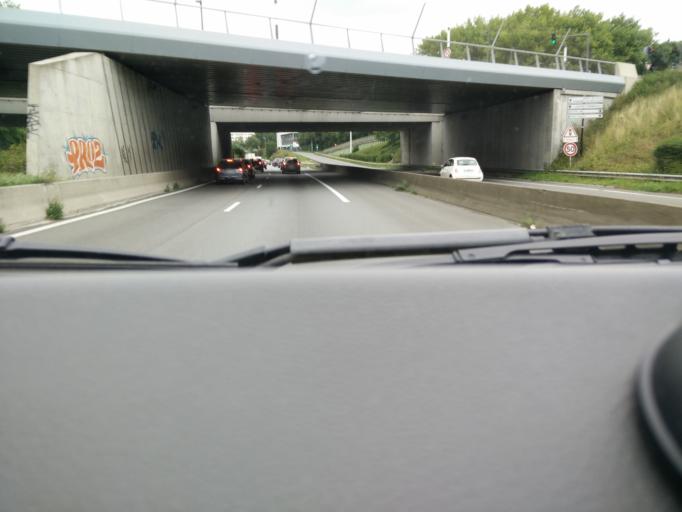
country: FR
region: Nord-Pas-de-Calais
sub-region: Departement du Nord
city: Lezennes
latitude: 50.6137
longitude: 3.1352
